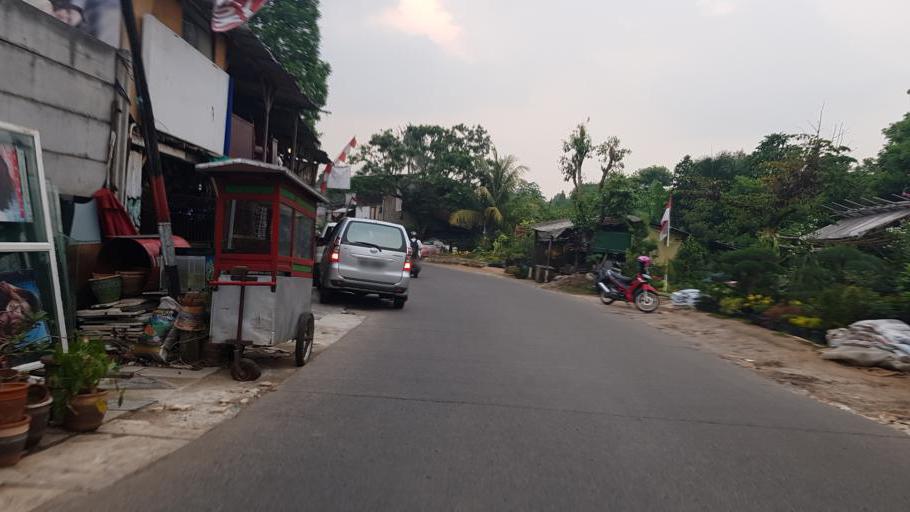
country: ID
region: West Java
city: Depok
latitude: -6.3693
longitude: 106.8116
